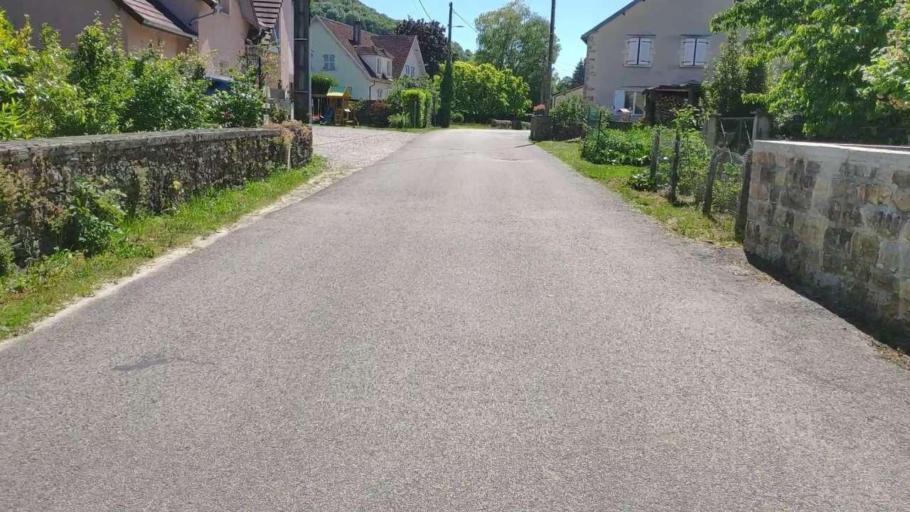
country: FR
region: Franche-Comte
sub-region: Departement du Jura
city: Perrigny
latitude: 46.7526
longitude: 5.6159
